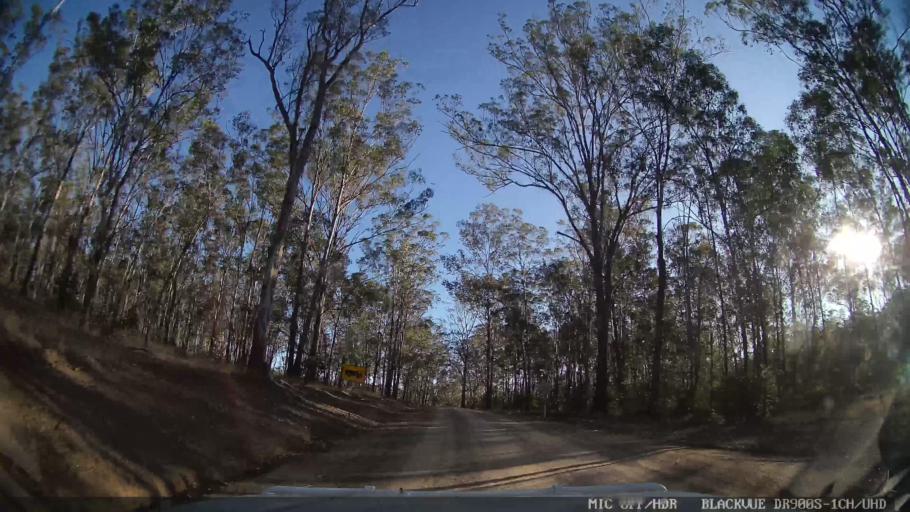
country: AU
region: Queensland
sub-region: Gladstone
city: Toolooa
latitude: -24.6821
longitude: 151.3327
